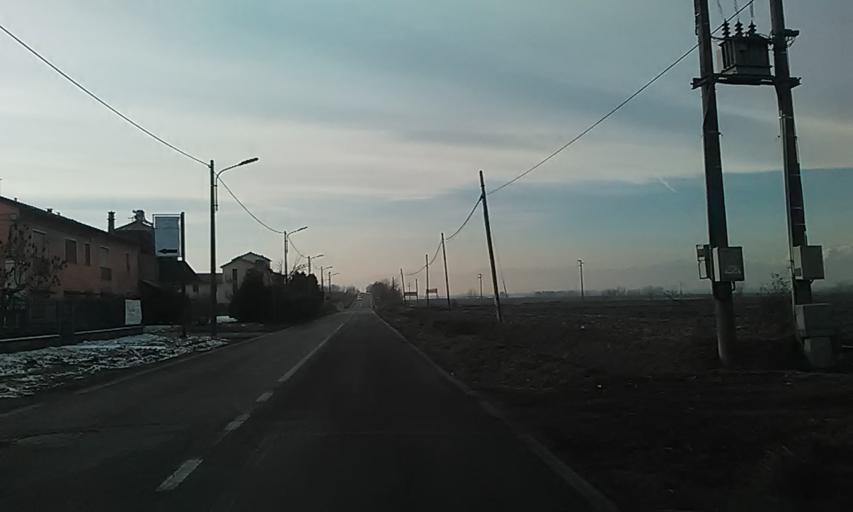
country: IT
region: Piedmont
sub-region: Provincia di Novara
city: Vicolungo
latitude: 45.4814
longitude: 8.4512
